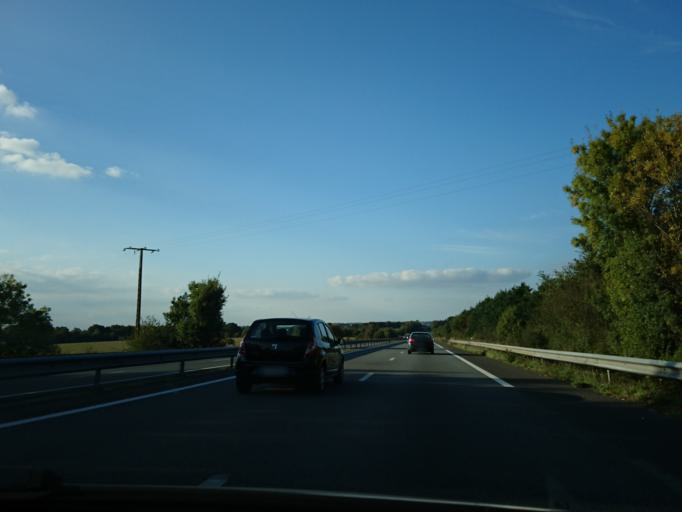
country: FR
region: Pays de la Loire
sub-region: Departement de la Loire-Atlantique
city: Derval
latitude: 47.6800
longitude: -1.6952
